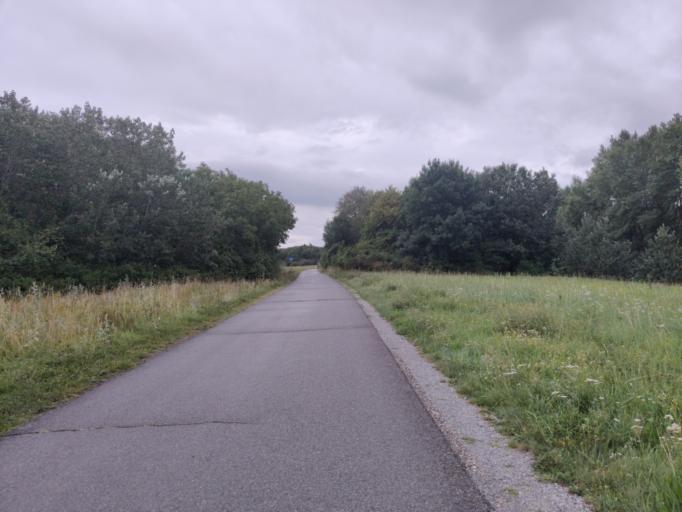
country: AT
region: Lower Austria
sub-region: Politischer Bezirk Korneuburg
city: Langenzersdorf
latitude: 48.2839
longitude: 16.3562
